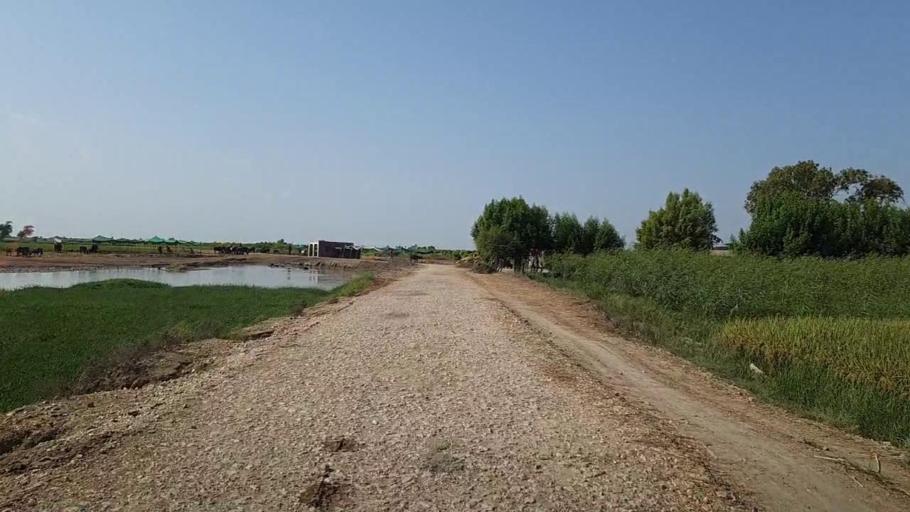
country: PK
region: Sindh
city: Kario
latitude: 24.7950
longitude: 68.5349
